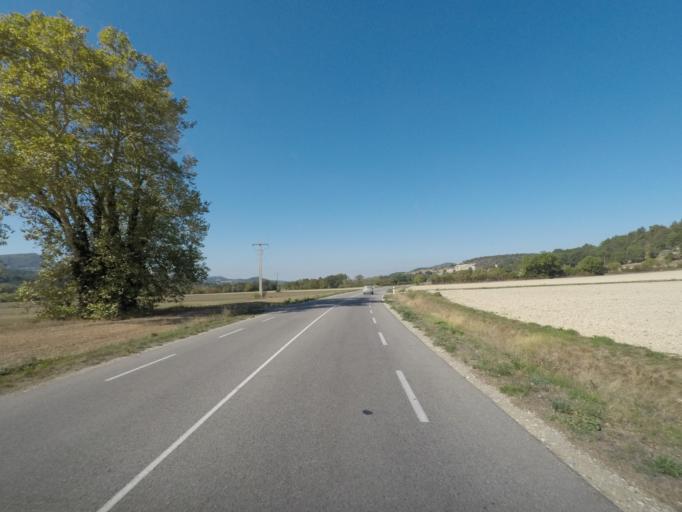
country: FR
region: Rhone-Alpes
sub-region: Departement de la Drome
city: Aouste-sur-Sye
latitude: 44.6990
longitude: 5.1269
